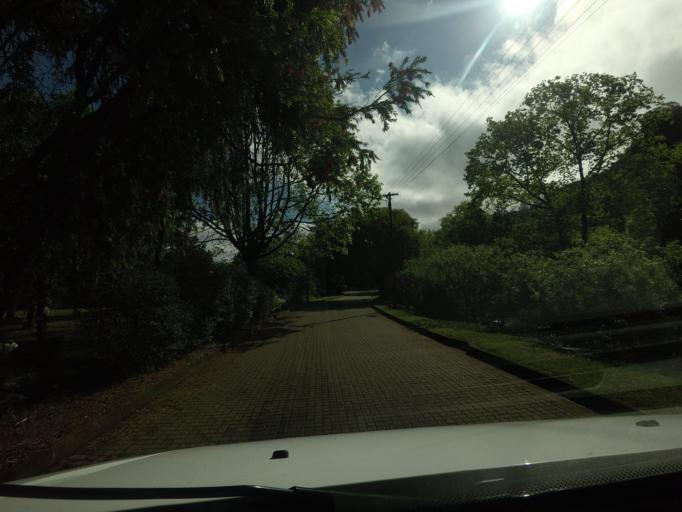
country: ZA
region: Mpumalanga
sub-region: Ehlanzeni District
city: Graksop
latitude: -25.0942
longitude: 30.7676
